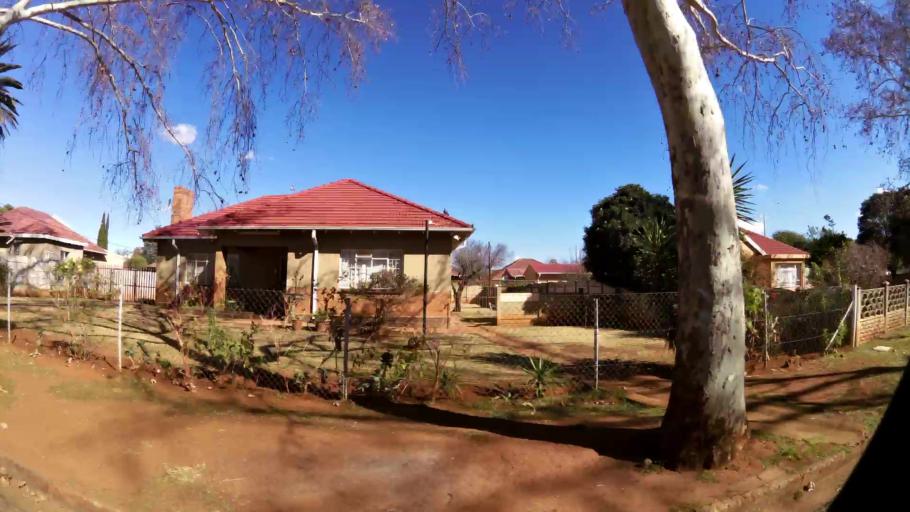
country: ZA
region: Gauteng
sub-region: West Rand District Municipality
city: Carletonville
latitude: -26.3637
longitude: 27.3993
